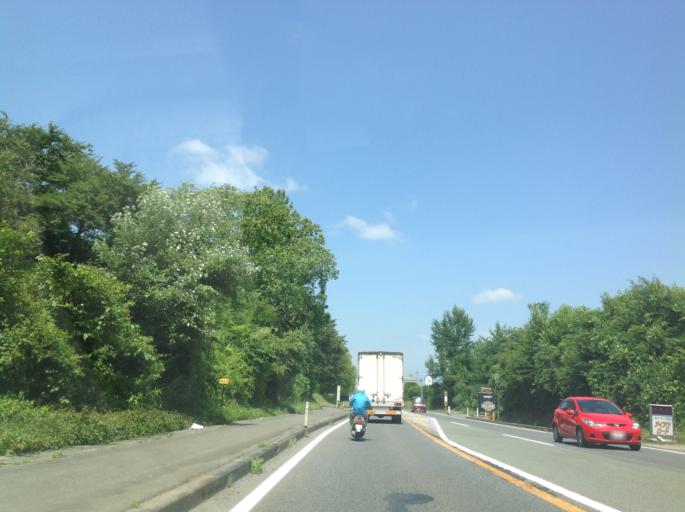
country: JP
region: Iwate
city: Hanamaki
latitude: 39.3515
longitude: 141.1096
